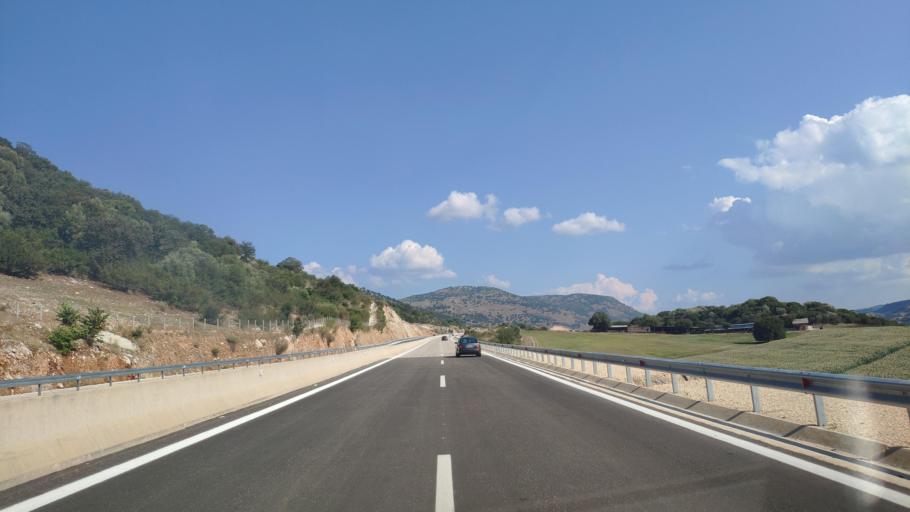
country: GR
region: West Greece
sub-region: Nomos Aitolias kai Akarnanias
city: Katouna
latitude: 38.8498
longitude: 21.0943
